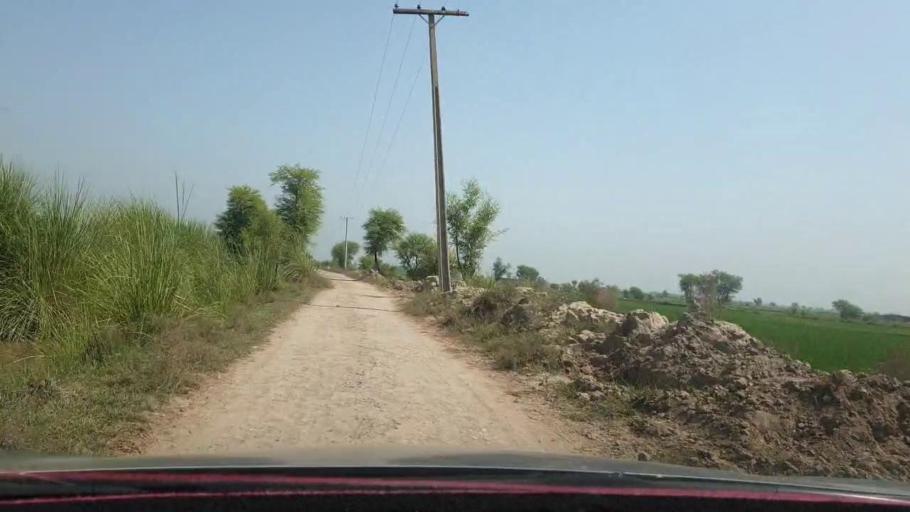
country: PK
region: Sindh
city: Warah
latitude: 27.4872
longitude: 67.8338
